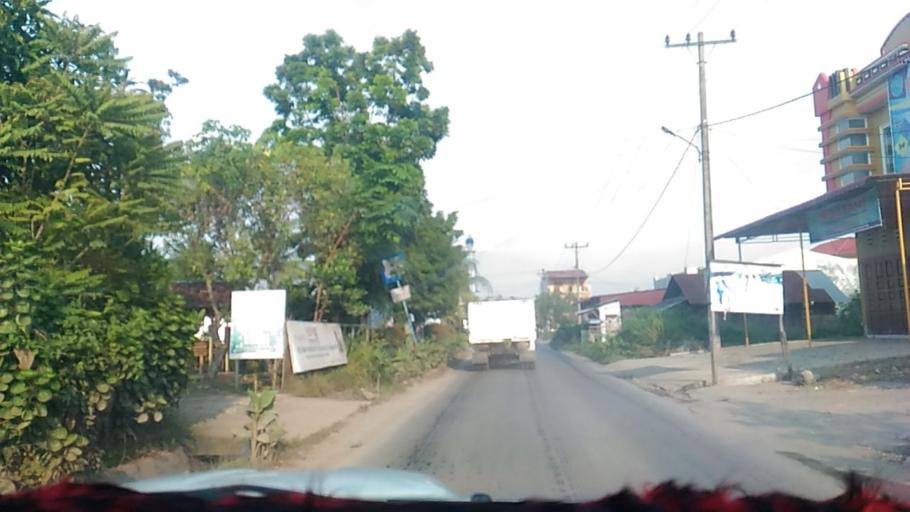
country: ID
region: North Sumatra
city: Labuhan Deli
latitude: 3.7070
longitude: 98.5996
